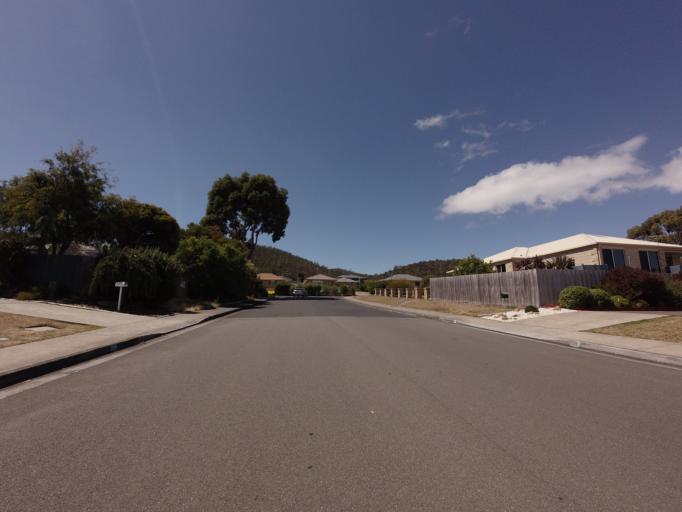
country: AU
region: Tasmania
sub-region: Clarence
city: Rokeby
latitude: -42.8994
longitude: 147.4559
